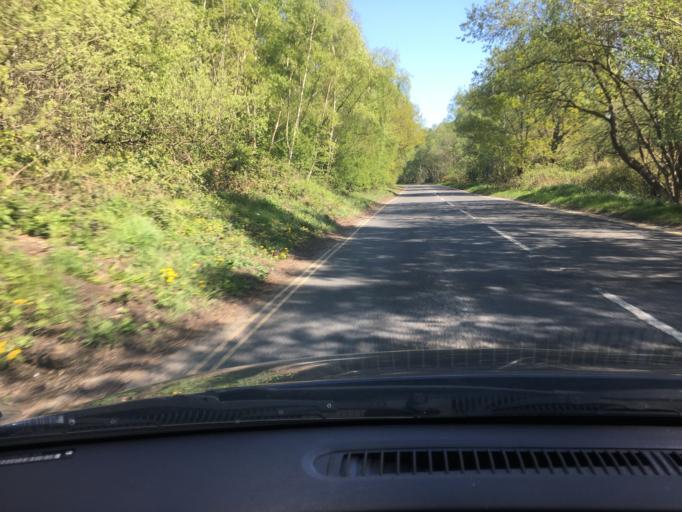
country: GB
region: England
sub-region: Hampshire
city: Yateley
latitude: 51.3248
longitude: -0.8304
